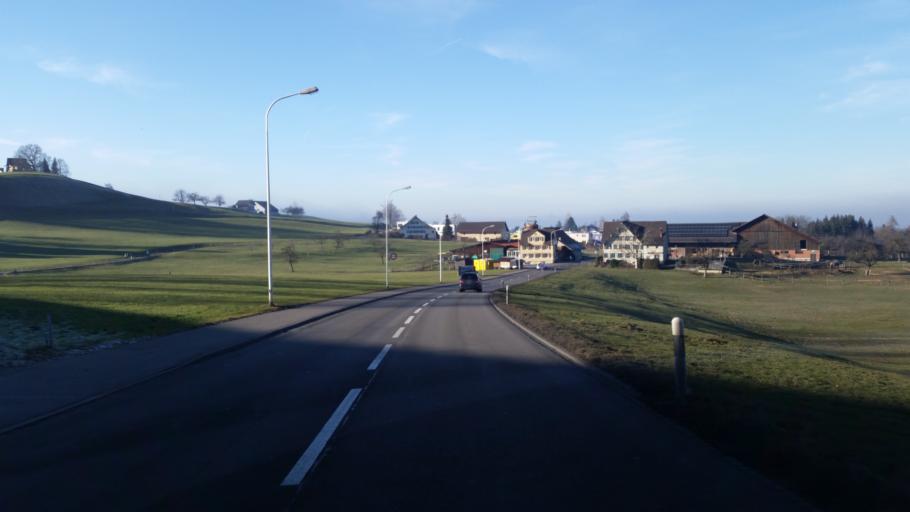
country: CH
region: Saint Gallen
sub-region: Wahlkreis St. Gallen
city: Gossau
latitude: 47.4022
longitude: 9.2577
